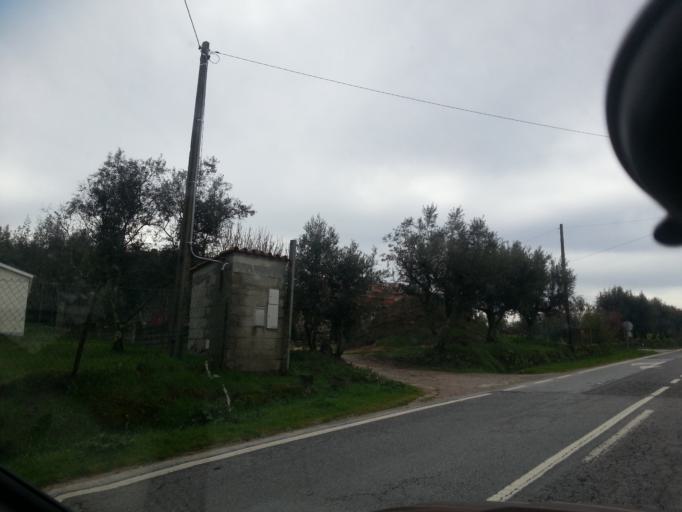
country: PT
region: Guarda
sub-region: Seia
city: Seia
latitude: 40.4797
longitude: -7.6660
